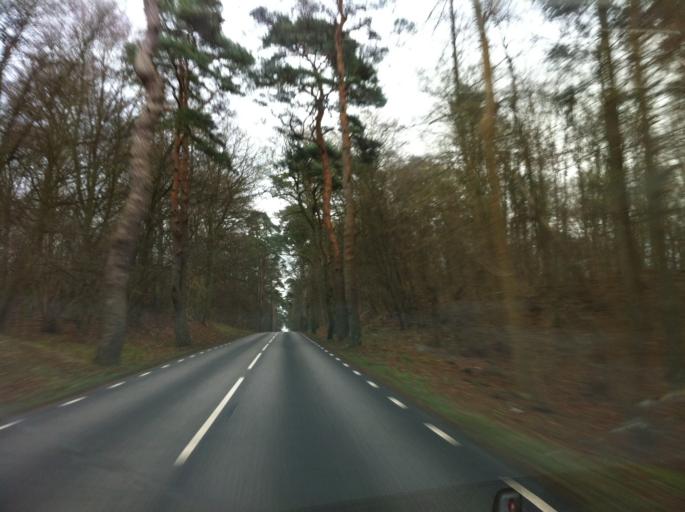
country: SE
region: Skane
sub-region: Sjobo Kommun
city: Sjoebo
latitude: 55.6918
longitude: 13.6173
